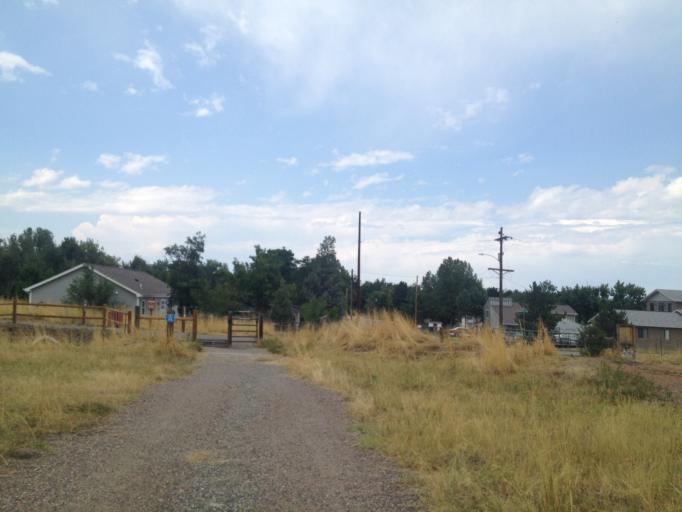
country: US
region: Colorado
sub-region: Boulder County
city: Superior
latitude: 39.9487
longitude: -105.1694
